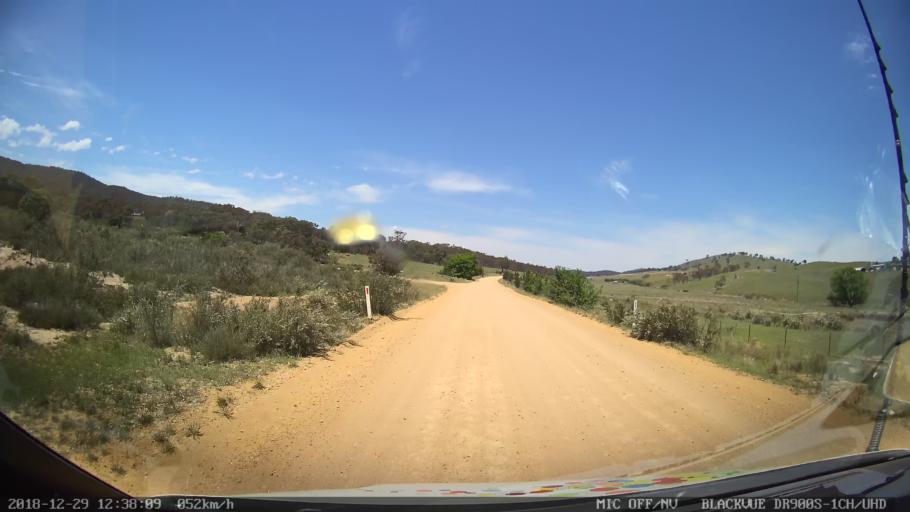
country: AU
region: Australian Capital Territory
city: Macarthur
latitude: -35.5863
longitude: 149.2292
